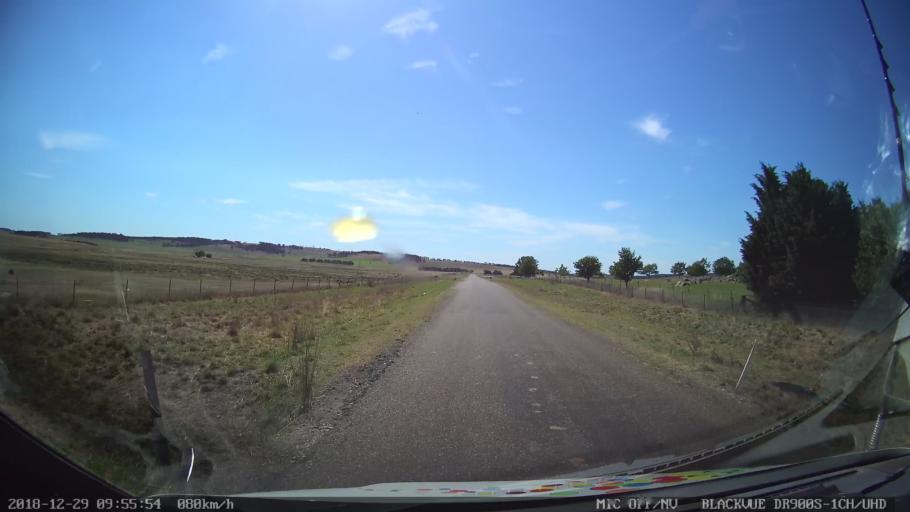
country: AU
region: New South Wales
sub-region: Goulburn Mulwaree
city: Goulburn
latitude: -34.7741
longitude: 149.4733
